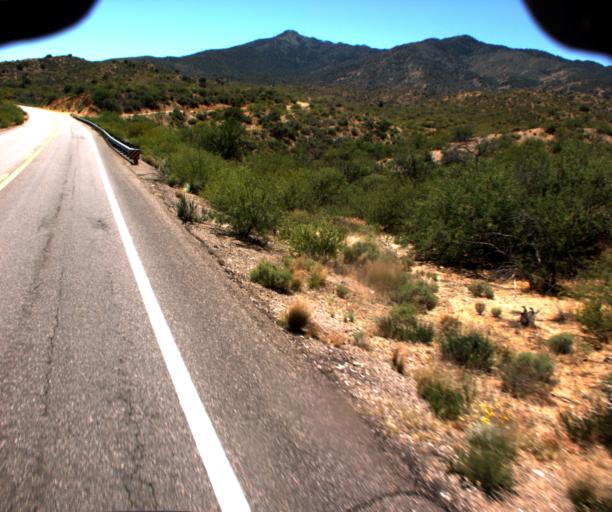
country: US
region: Arizona
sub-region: Gila County
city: Globe
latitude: 33.3185
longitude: -110.7362
